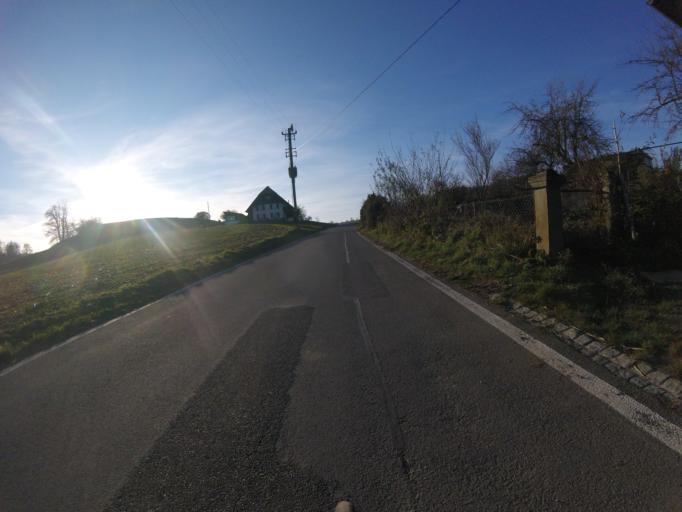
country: CH
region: Bern
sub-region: Bern-Mittelland District
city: Frauenkappelen
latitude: 46.9397
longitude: 7.3042
